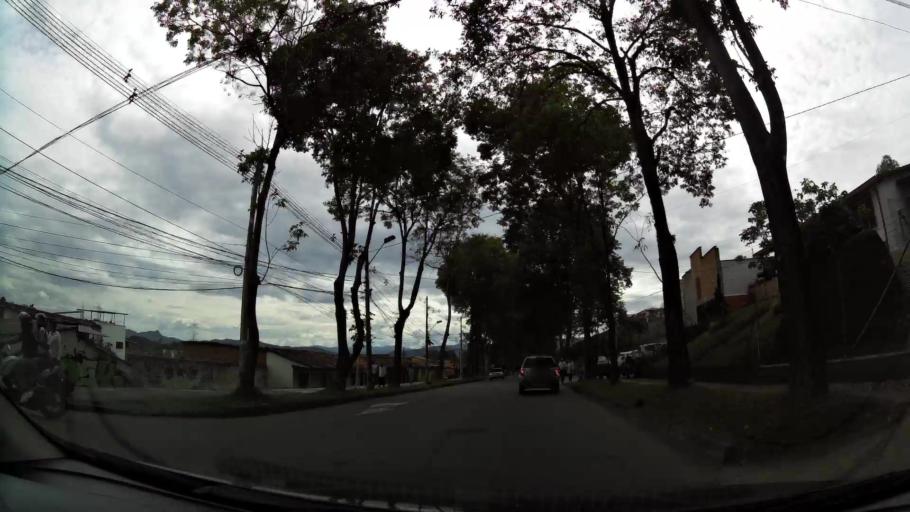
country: CO
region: Antioquia
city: Rionegro
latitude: 6.1519
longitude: -75.3802
